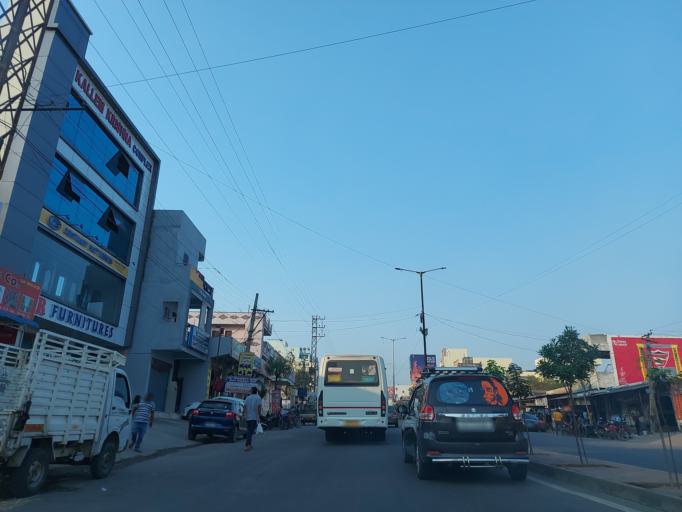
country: IN
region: Telangana
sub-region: Rangareddi
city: Balapur
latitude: 17.2053
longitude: 78.4763
